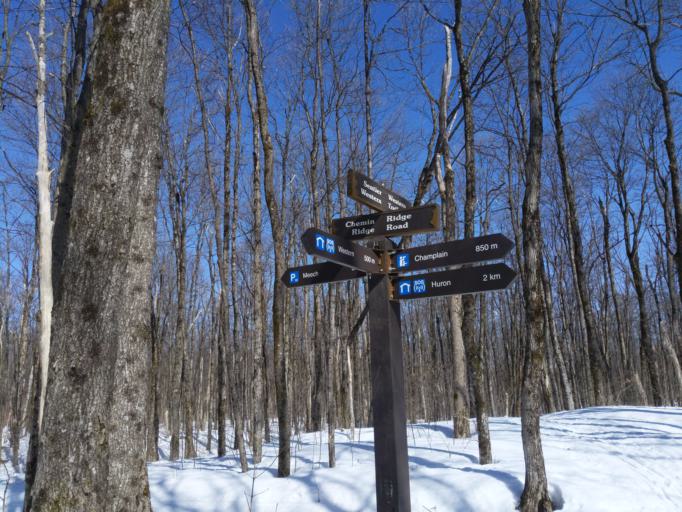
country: CA
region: Quebec
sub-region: Outaouais
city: Wakefield
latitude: 45.5151
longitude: -75.9122
